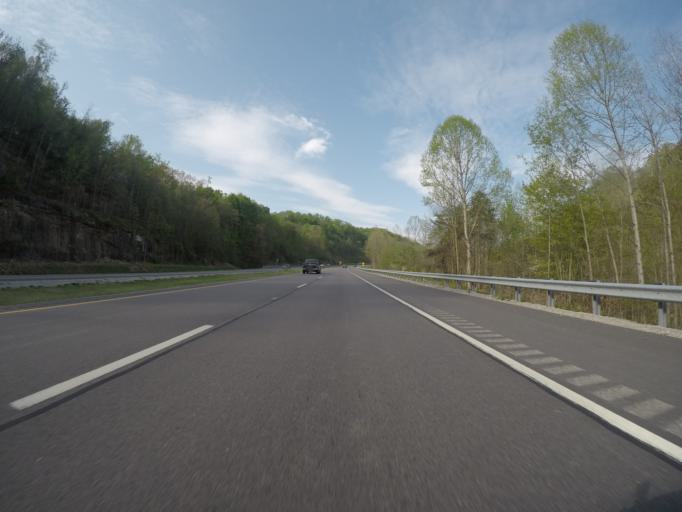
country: US
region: West Virginia
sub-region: Kanawha County
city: Dunbar
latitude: 38.3024
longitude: -81.7382
